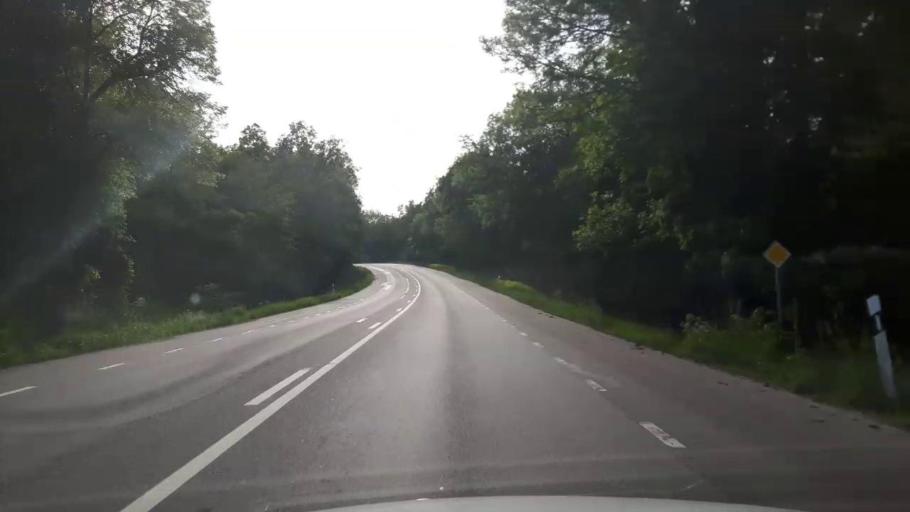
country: SE
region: Uppsala
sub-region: Enkopings Kommun
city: Orsundsbro
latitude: 59.6527
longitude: 17.3766
